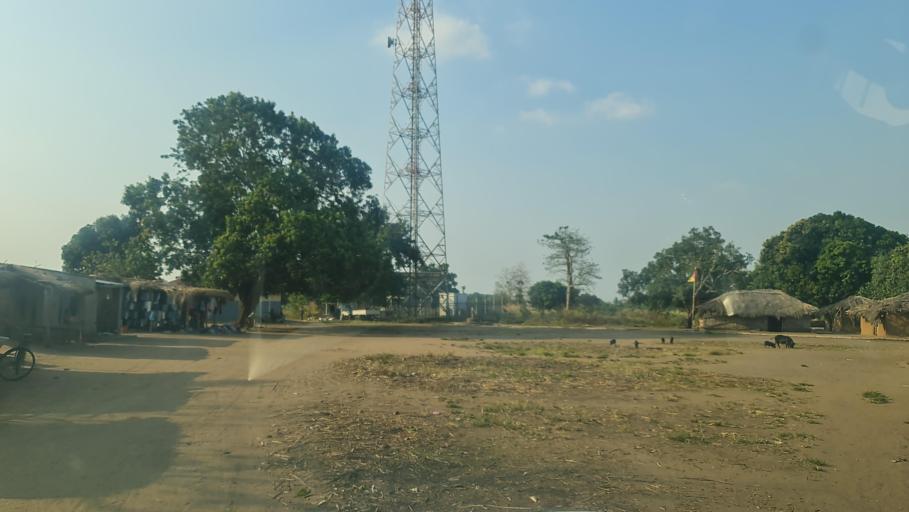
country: MZ
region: Zambezia
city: Quelimane
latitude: -18.1440
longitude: 35.9868
